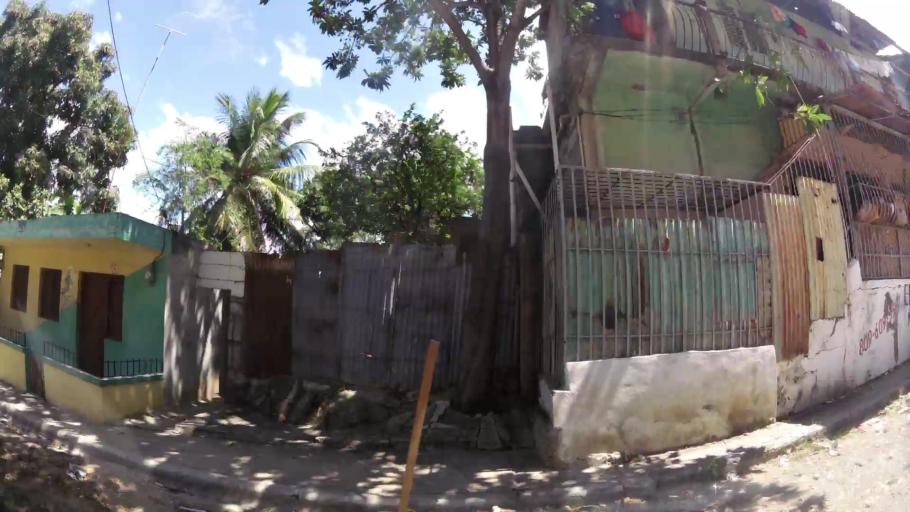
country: DO
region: San Cristobal
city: San Cristobal
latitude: 18.4051
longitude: -70.1155
